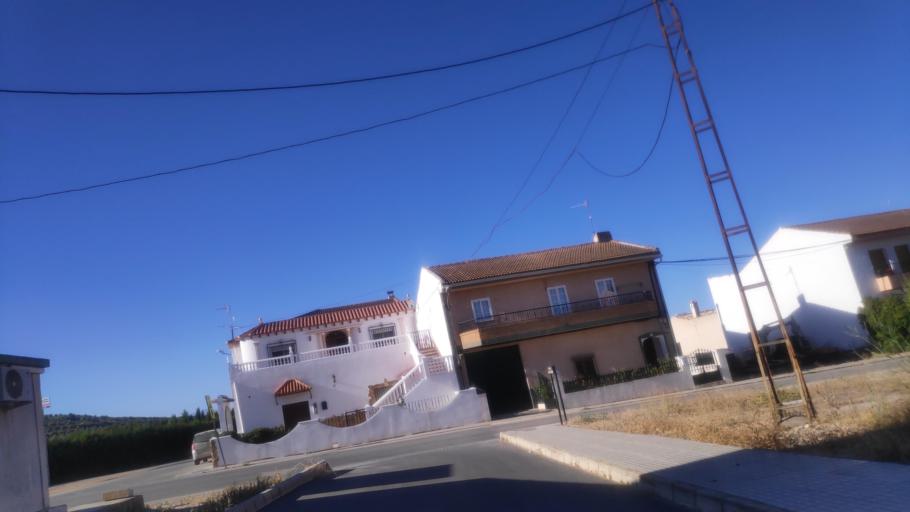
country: ES
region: Andalusia
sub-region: Provincia de Jaen
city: Pozo Alcon
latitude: 37.6719
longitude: -2.9681
